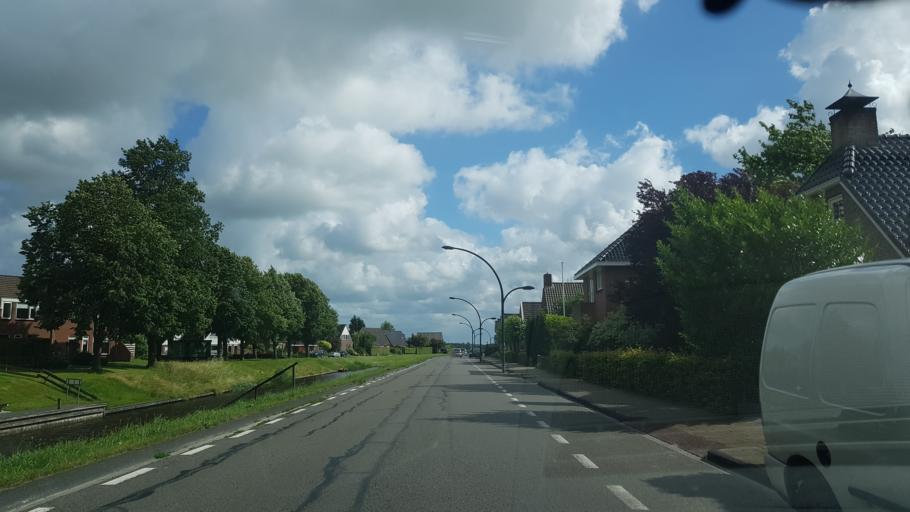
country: NL
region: Groningen
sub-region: Gemeente Bedum
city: Bedum
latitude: 53.4028
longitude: 6.6762
